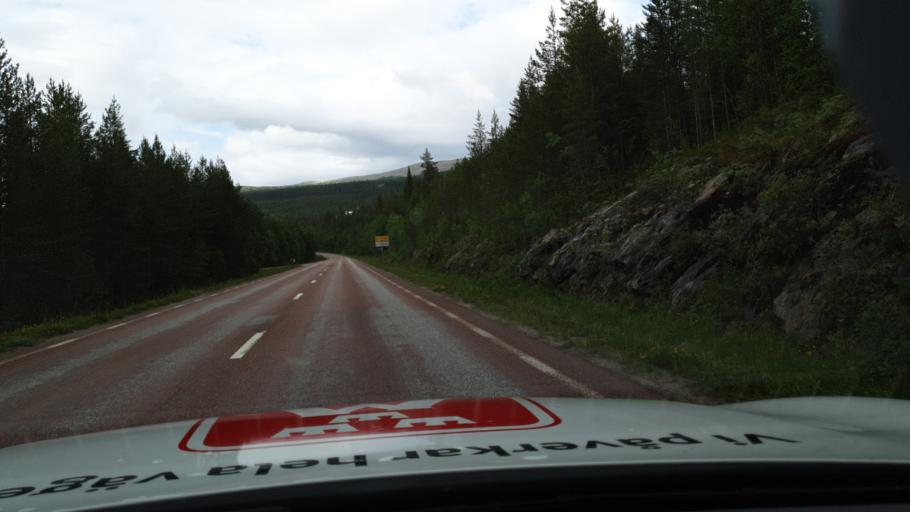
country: SE
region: Jaemtland
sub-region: Bergs Kommun
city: Hoverberg
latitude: 62.4878
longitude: 13.9175
